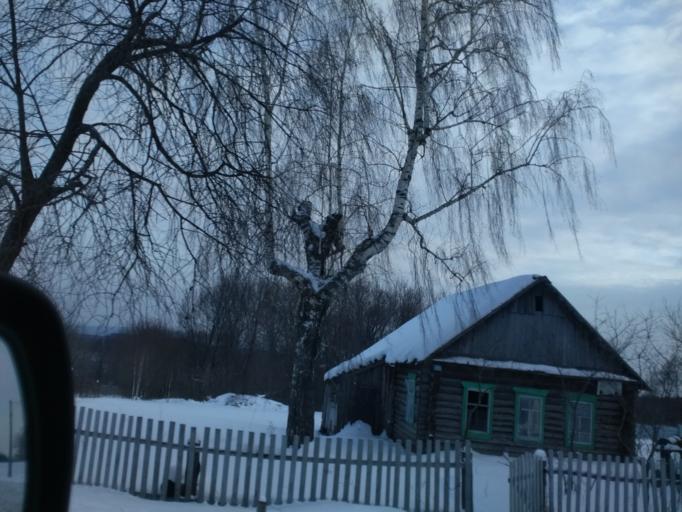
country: RU
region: Bashkortostan
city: Kudeyevskiy
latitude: 54.7371
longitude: 56.6045
